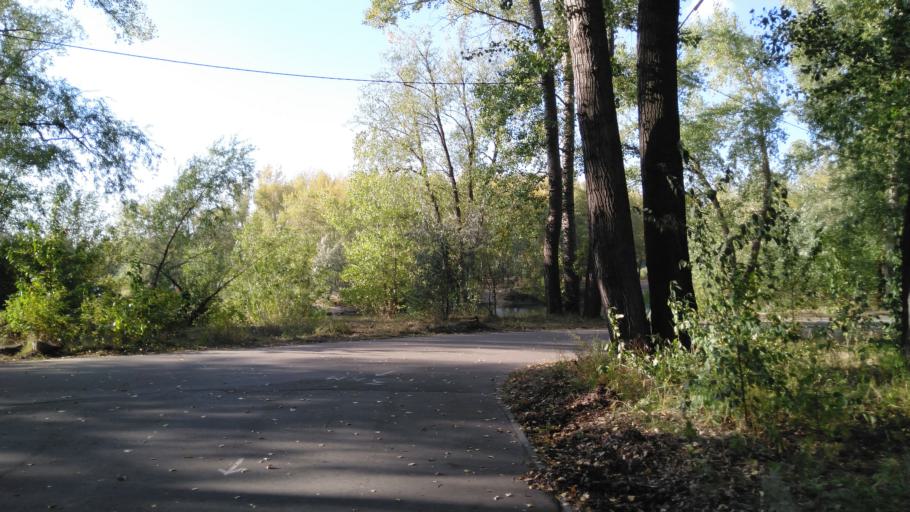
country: KZ
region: Pavlodar
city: Pavlodar
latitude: 52.2644
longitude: 76.9313
